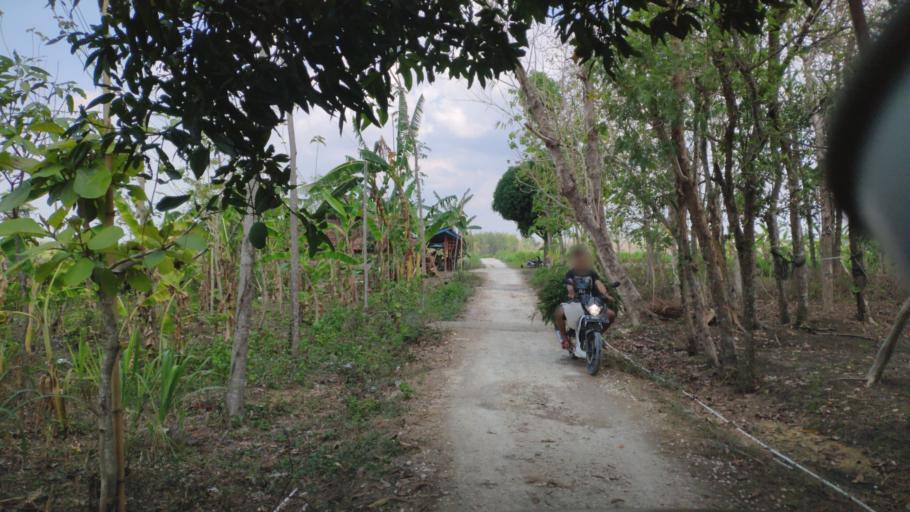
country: ID
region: Central Java
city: Sambirejo
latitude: -7.0554
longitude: 111.3410
